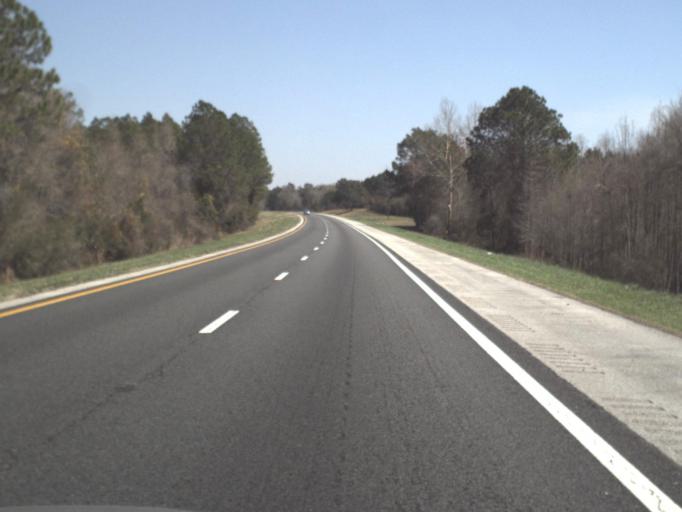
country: US
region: Florida
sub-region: Holmes County
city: Bonifay
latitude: 30.7597
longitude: -85.7341
